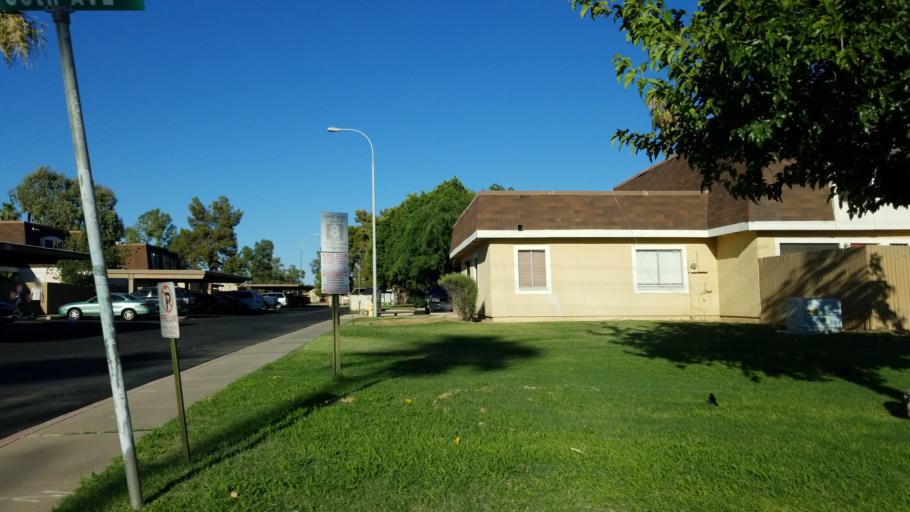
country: US
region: Arizona
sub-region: Maricopa County
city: Glendale
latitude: 33.5583
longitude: -112.1342
